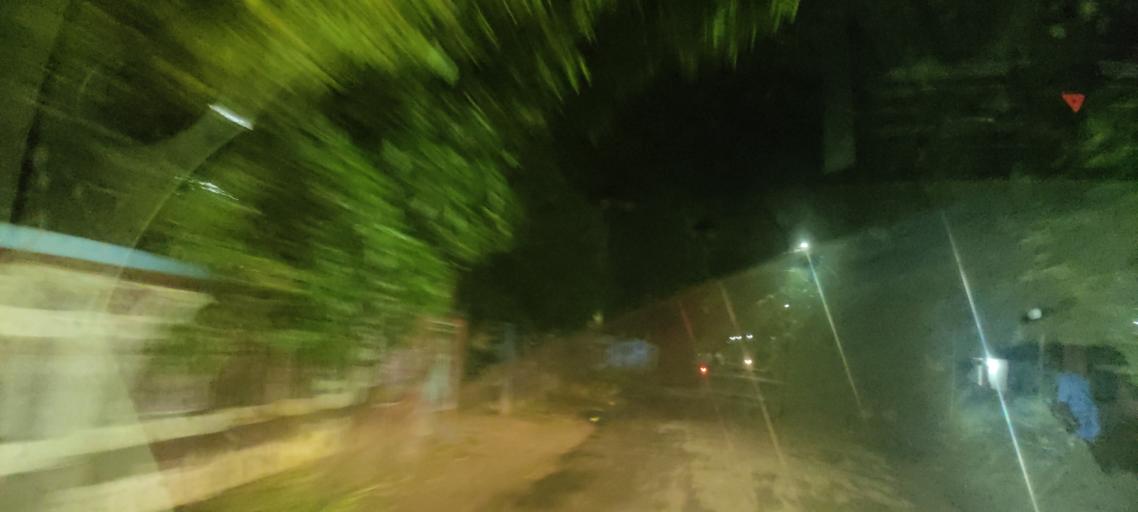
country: IN
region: Kerala
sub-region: Alappuzha
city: Vayalar
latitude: 9.7238
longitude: 76.3325
